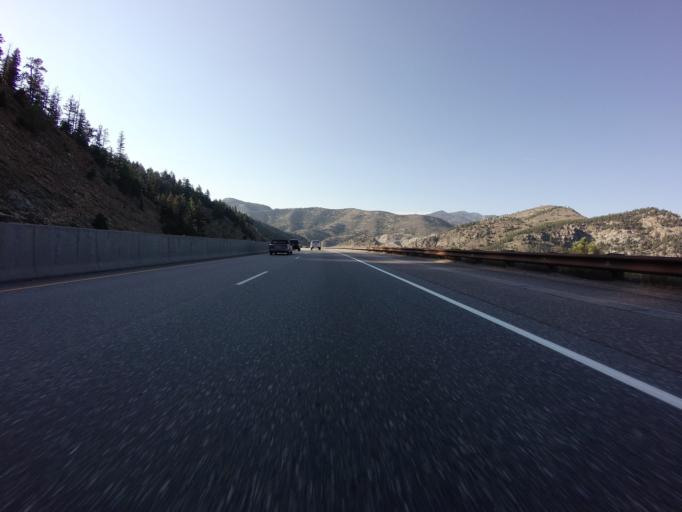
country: US
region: Colorado
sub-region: Clear Creek County
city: Idaho Springs
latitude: 39.7329
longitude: -105.4275
